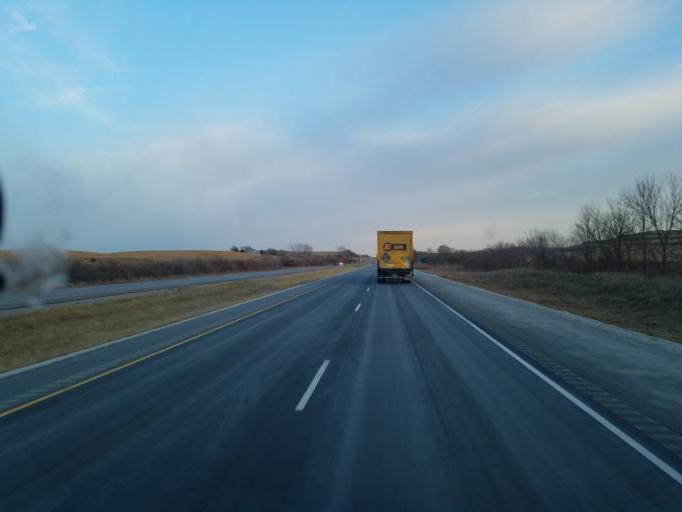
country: US
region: Iowa
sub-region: Harrison County
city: Logan
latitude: 41.4981
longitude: -95.6780
